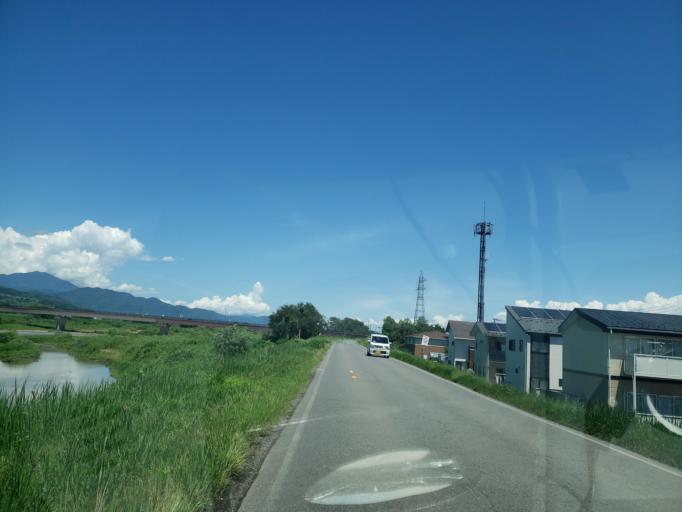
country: JP
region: Nagano
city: Nagano-shi
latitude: 36.5362
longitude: 138.1151
